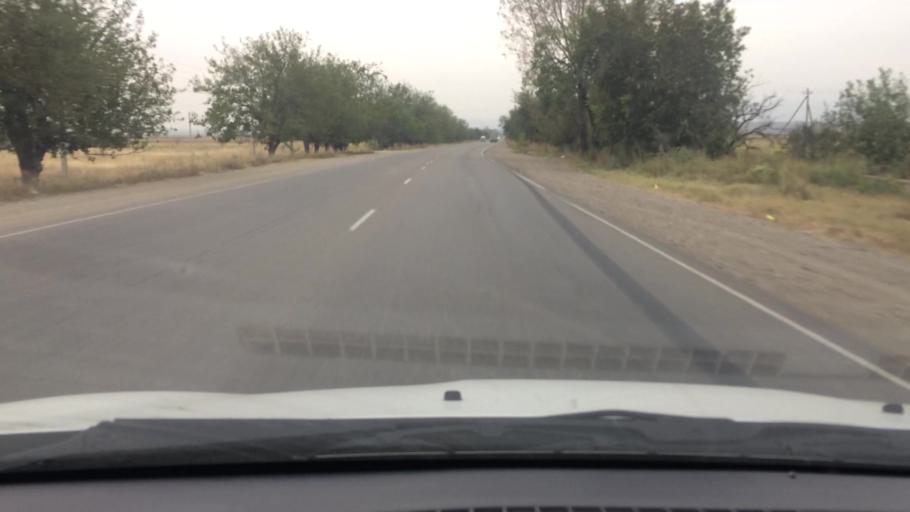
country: GE
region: Kvemo Kartli
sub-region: Marneuli
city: Marneuli
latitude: 41.5677
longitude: 44.7753
